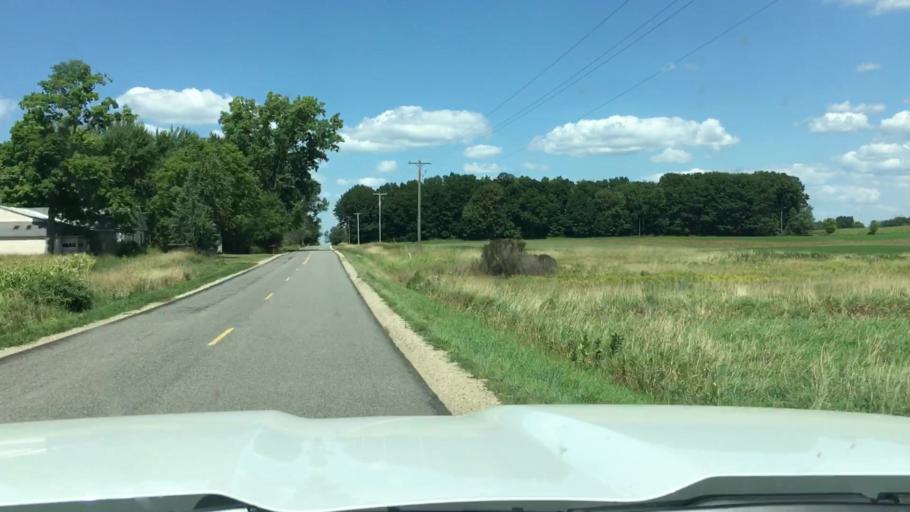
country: US
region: Michigan
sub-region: Muskegon County
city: Ravenna
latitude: 43.2530
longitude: -85.9180
